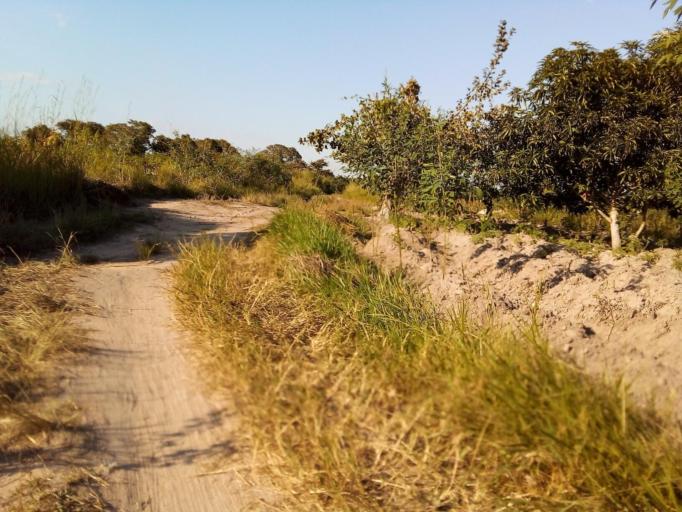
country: MZ
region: Zambezia
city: Quelimane
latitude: -17.5501
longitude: 36.7085
